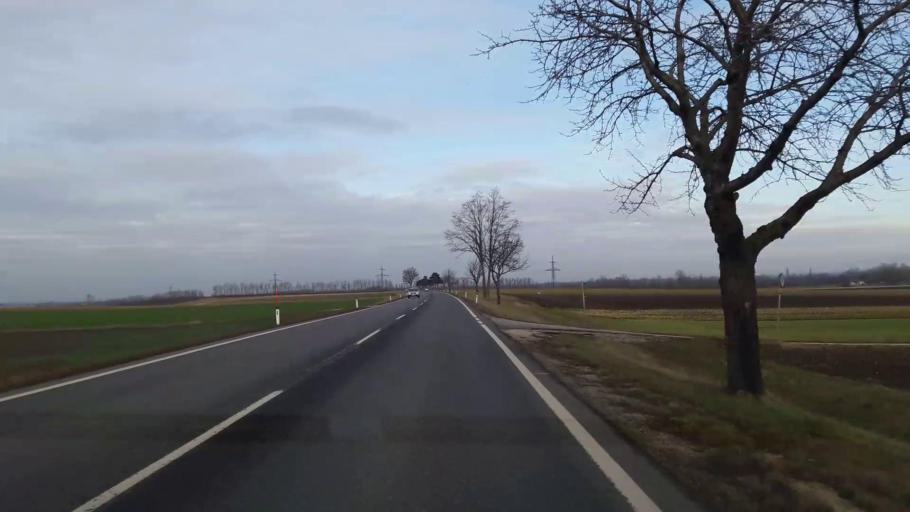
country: AT
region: Lower Austria
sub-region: Politischer Bezirk Mistelbach
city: Staatz
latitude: 48.6981
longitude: 16.4428
